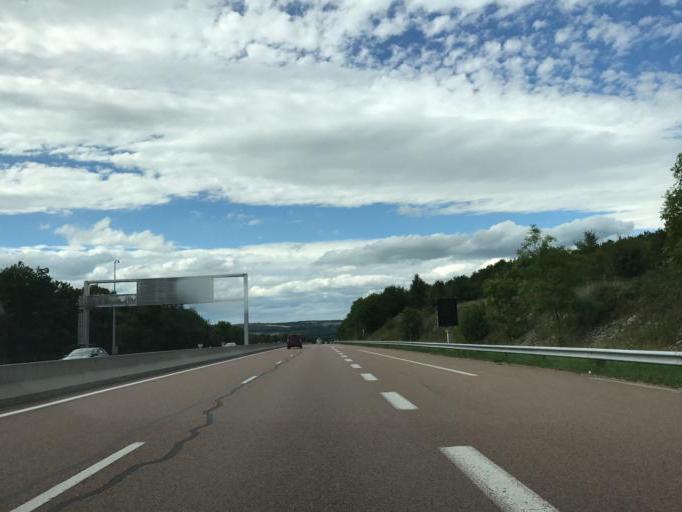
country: FR
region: Bourgogne
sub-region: Departement de la Cote-d'Or
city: Savigny-les-Beaune
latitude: 47.1183
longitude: 4.7061
